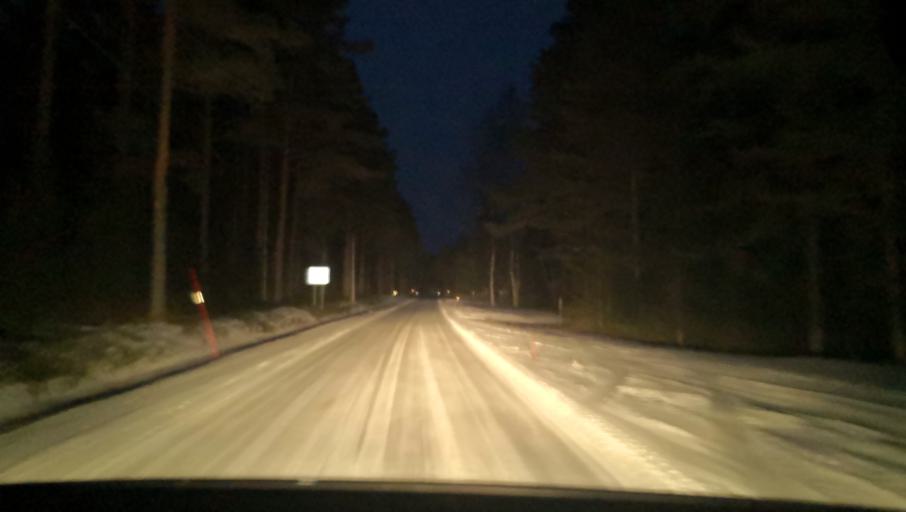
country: SE
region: Uppsala
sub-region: Heby Kommun
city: Tarnsjo
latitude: 60.2814
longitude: 16.8040
